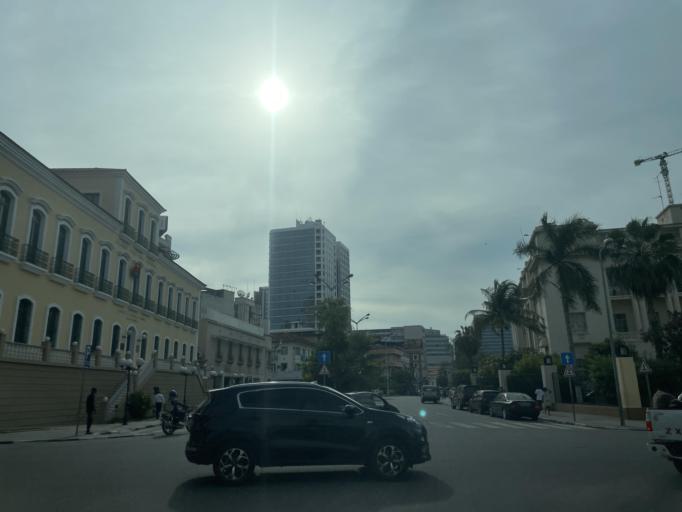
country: AO
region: Luanda
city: Luanda
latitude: -8.8131
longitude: 13.2347
